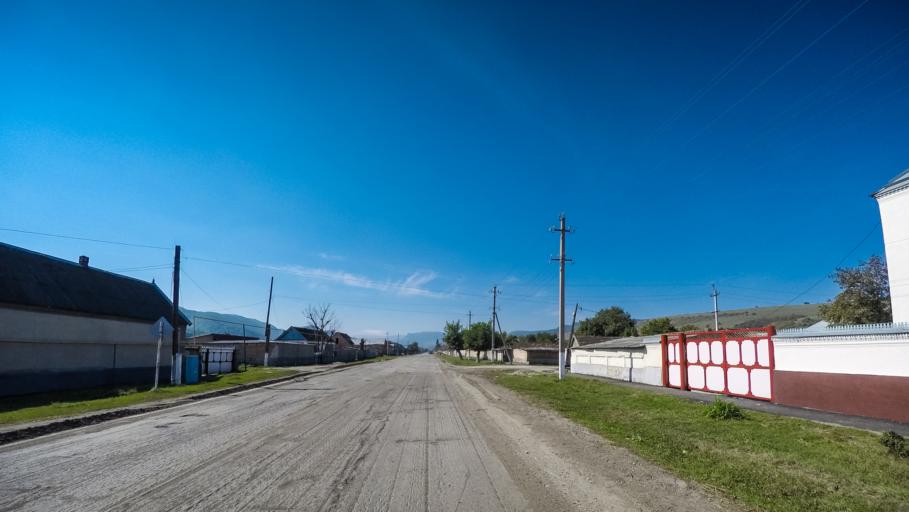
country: RU
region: Kabardino-Balkariya
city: Lechinkay
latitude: 43.5623
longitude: 43.4488
